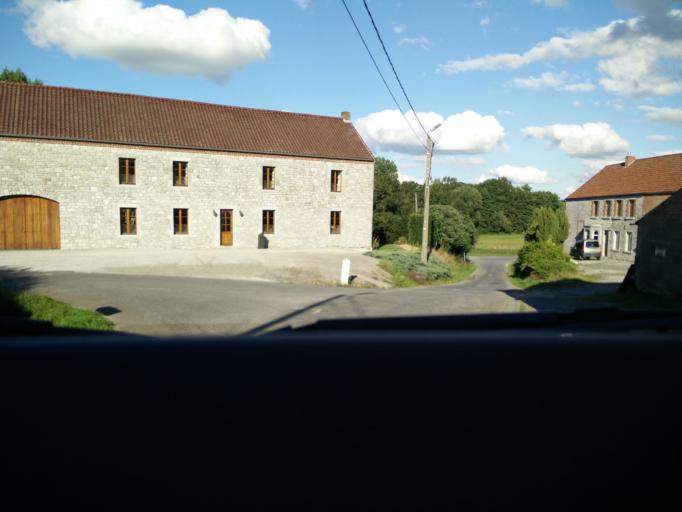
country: BE
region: Wallonia
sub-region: Province du Hainaut
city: Beaumont
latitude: 50.1854
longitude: 4.2656
